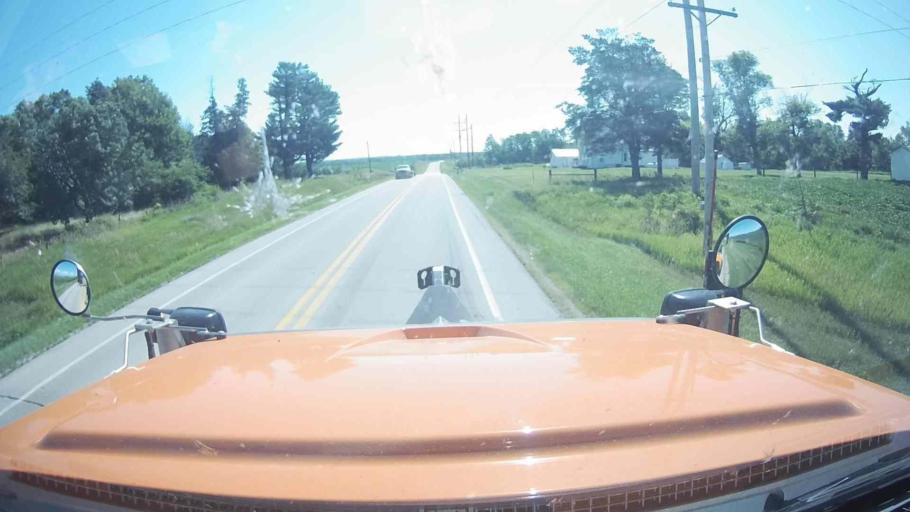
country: US
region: Iowa
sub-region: Benton County
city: Belle Plaine
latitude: 41.8444
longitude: -92.2695
